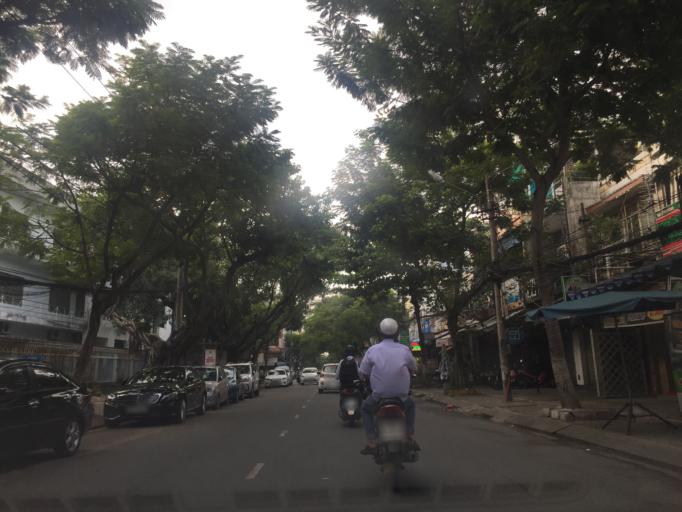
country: VN
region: Da Nang
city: Da Nang
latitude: 16.0784
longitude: 108.2118
